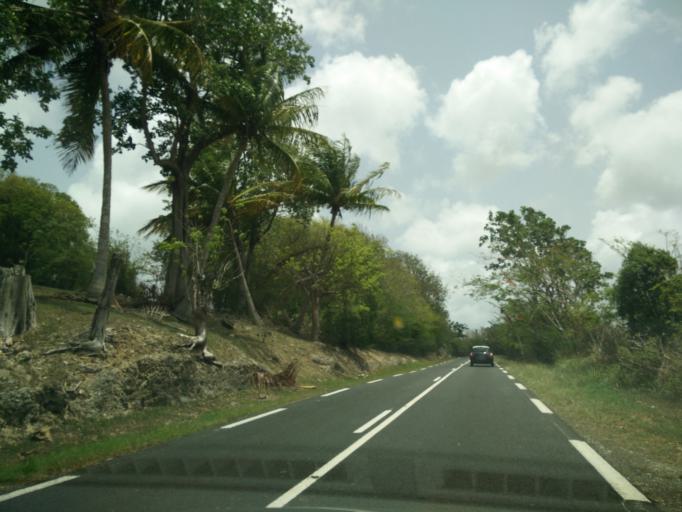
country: GP
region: Guadeloupe
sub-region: Guadeloupe
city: Petit-Canal
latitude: 16.4019
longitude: -61.5035
